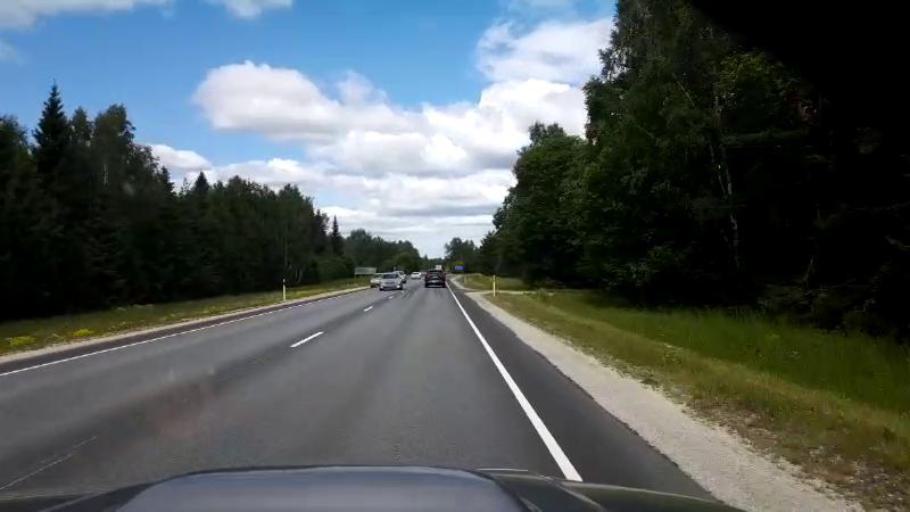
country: EE
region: Harju
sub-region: Nissi vald
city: Riisipere
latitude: 59.0981
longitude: 24.4684
